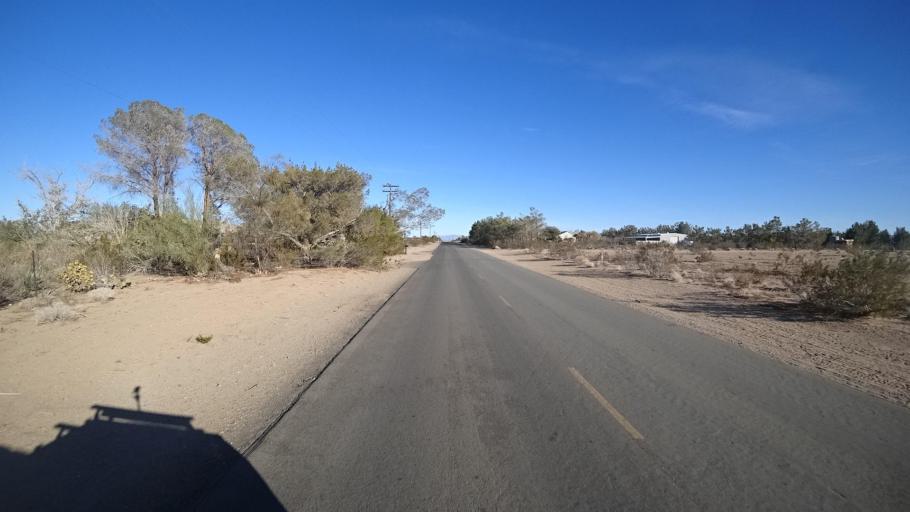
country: US
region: California
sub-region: Kern County
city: Ridgecrest
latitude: 35.6299
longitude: -117.7173
